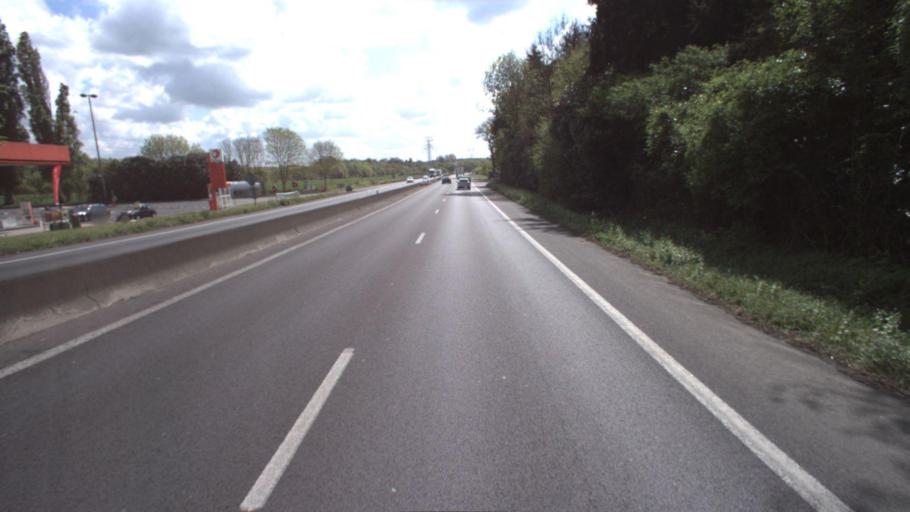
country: FR
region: Ile-de-France
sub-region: Departement de Seine-et-Marne
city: Ozoir-la-Ferriere
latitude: 48.7669
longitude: 2.6495
